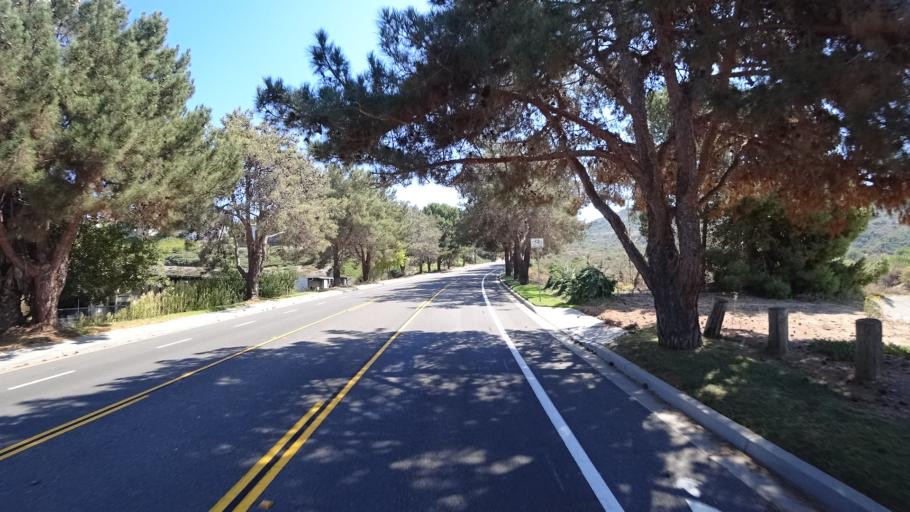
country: US
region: California
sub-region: Orange County
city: San Clemente
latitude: 33.4397
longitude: -117.6007
